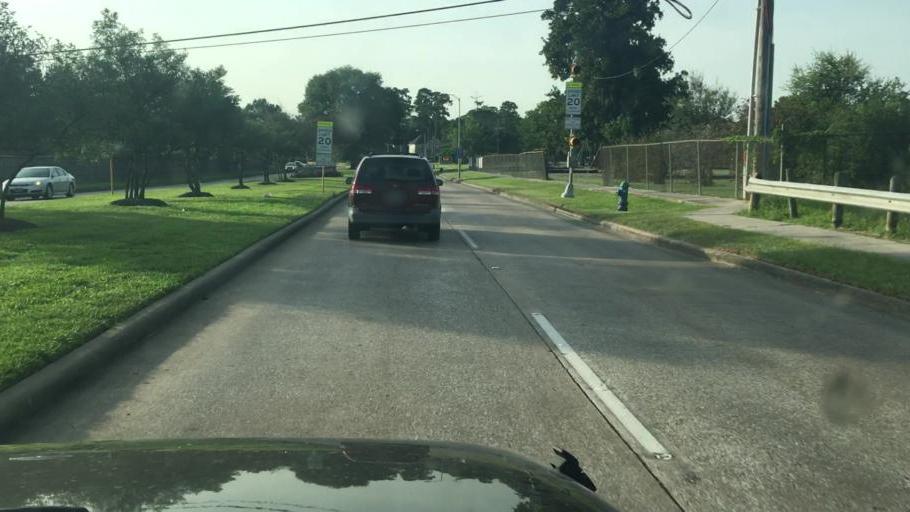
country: US
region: Texas
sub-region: Harris County
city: Atascocita
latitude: 30.0022
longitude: -95.1636
